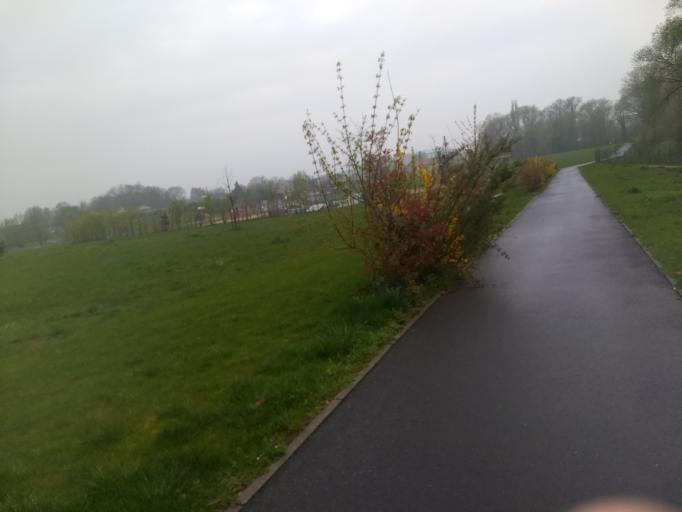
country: FR
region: Nord-Pas-de-Calais
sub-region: Departement du Pas-de-Calais
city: Biache-Saint-Vaast
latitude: 50.3086
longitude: 2.9551
